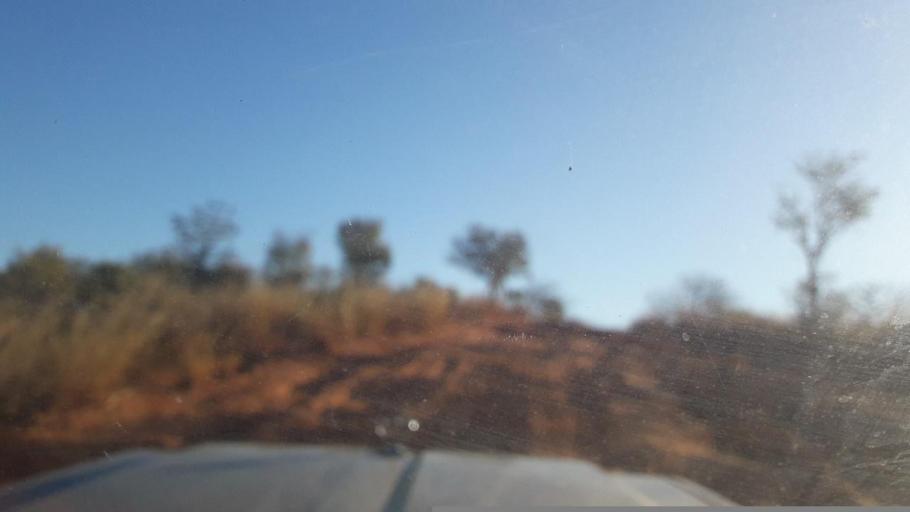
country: MG
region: Boeny
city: Sitampiky
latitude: -16.4974
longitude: 45.6072
